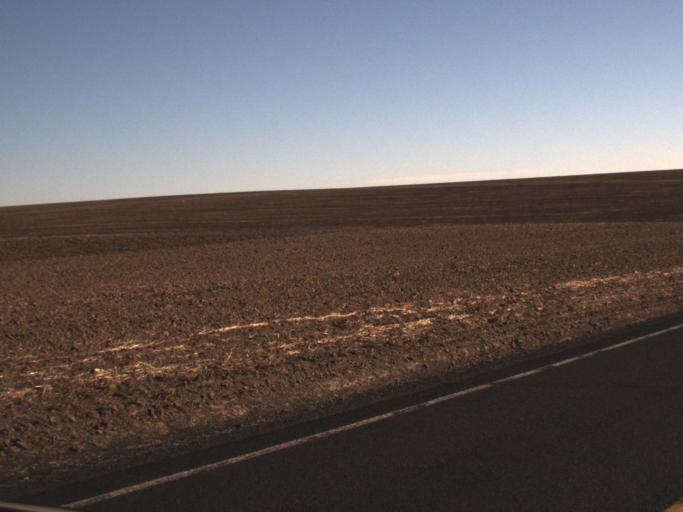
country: US
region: Washington
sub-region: Adams County
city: Ritzville
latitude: 47.0950
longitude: -118.3654
